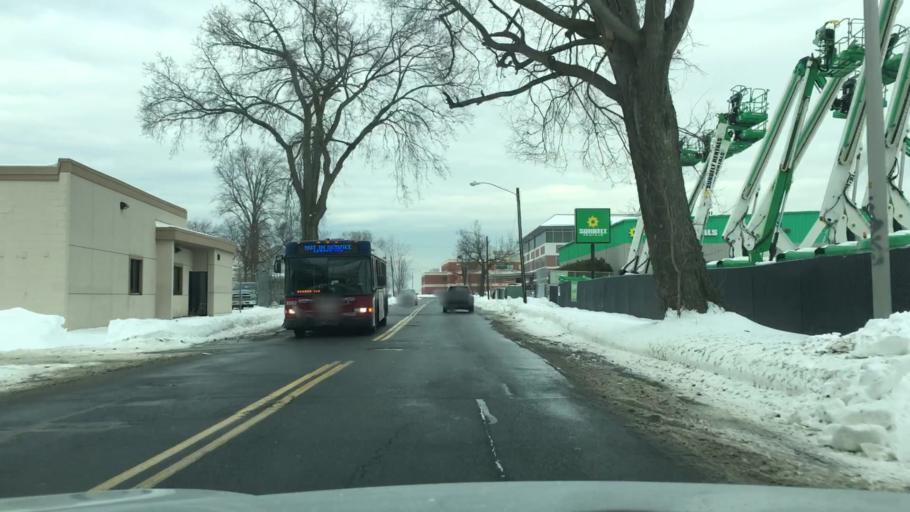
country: US
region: Massachusetts
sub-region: Hampden County
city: West Springfield
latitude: 42.1221
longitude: -72.6133
